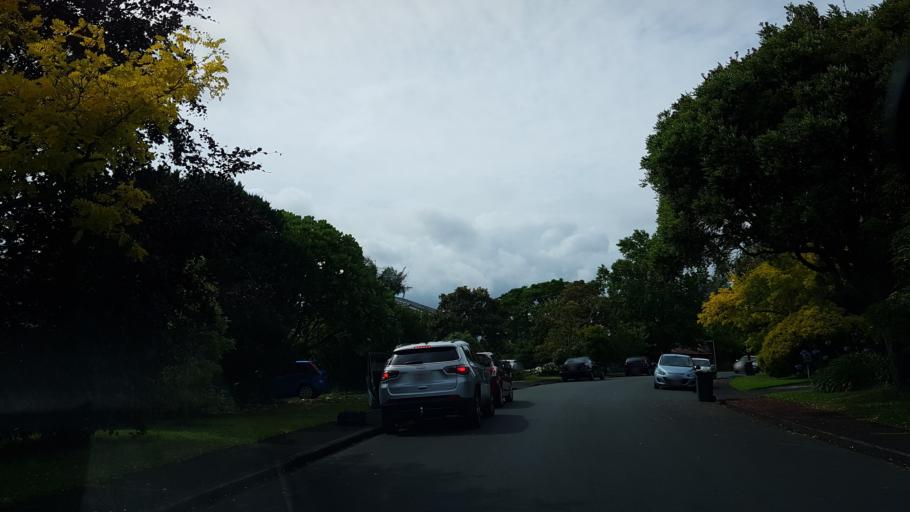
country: NZ
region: Auckland
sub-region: Auckland
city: North Shore
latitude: -36.7889
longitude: 174.7467
